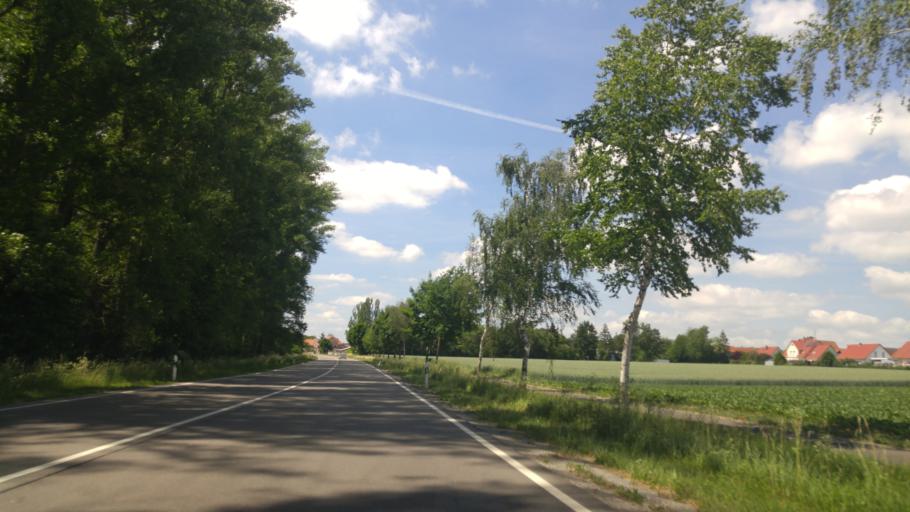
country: DE
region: Bavaria
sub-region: Regierungsbezirk Mittelfranken
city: Gallmersgarten
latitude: 49.4535
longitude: 10.2813
